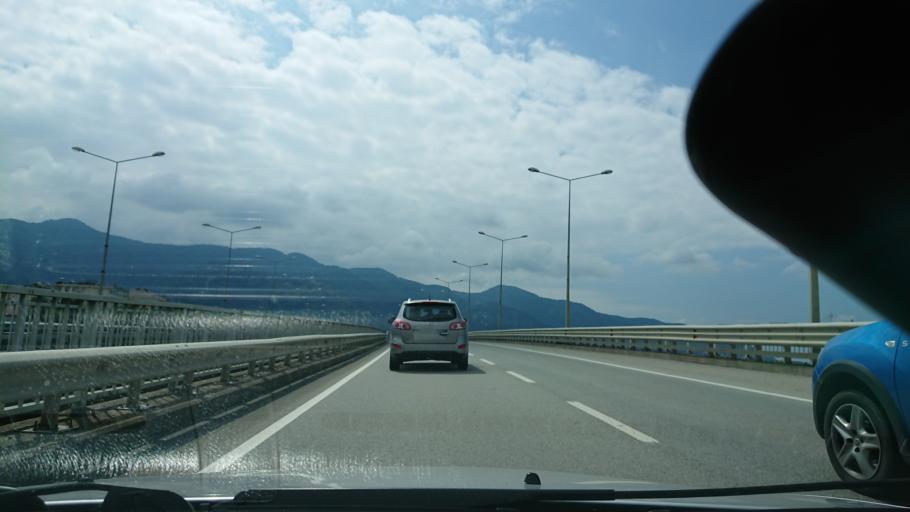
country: TR
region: Trabzon
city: Espiye
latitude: 40.9502
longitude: 38.7074
